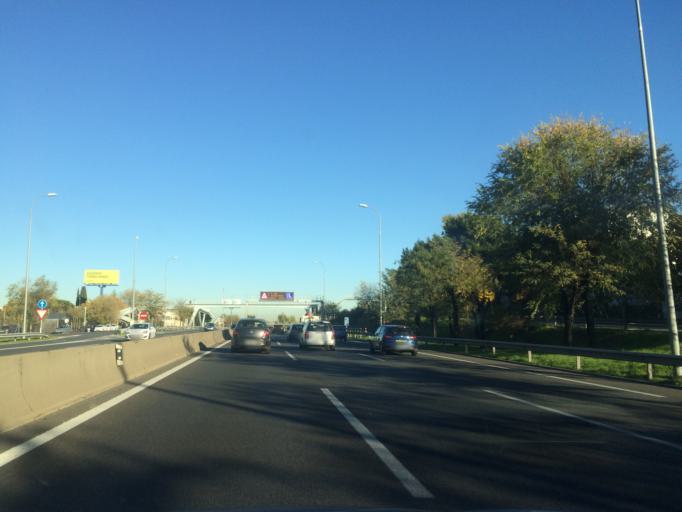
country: ES
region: Madrid
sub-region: Provincia de Madrid
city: San Blas
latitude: 40.4499
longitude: -3.6030
